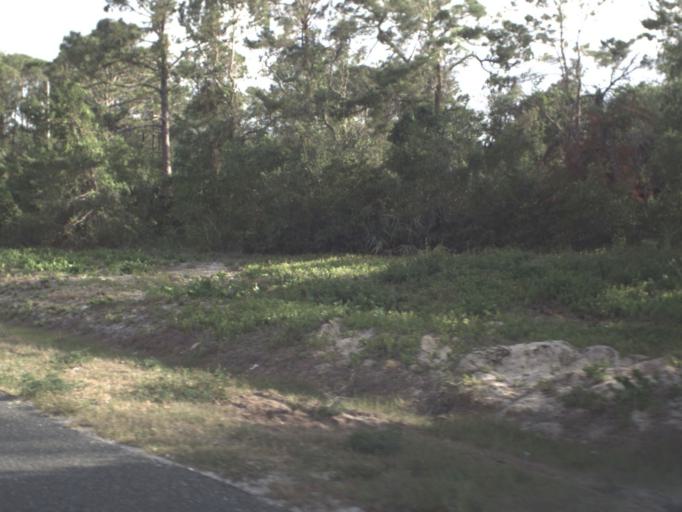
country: US
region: Florida
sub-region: Brevard County
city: Mims
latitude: 28.7317
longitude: -80.8662
